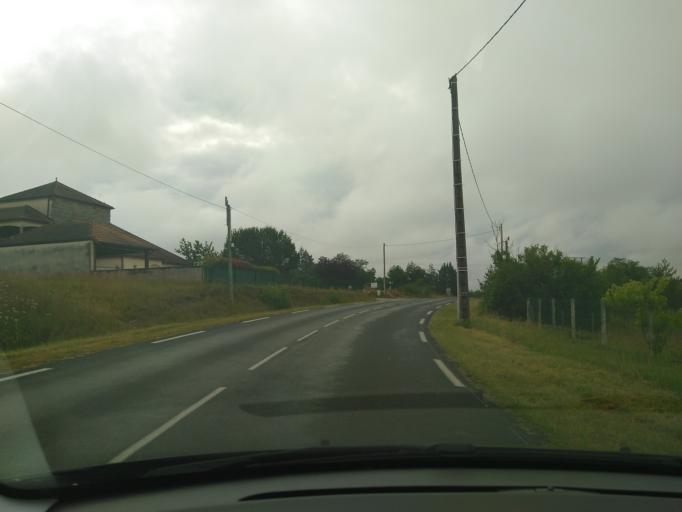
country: FR
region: Limousin
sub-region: Departement de la Correze
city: Brive-la-Gaillarde
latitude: 45.1040
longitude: 1.5341
